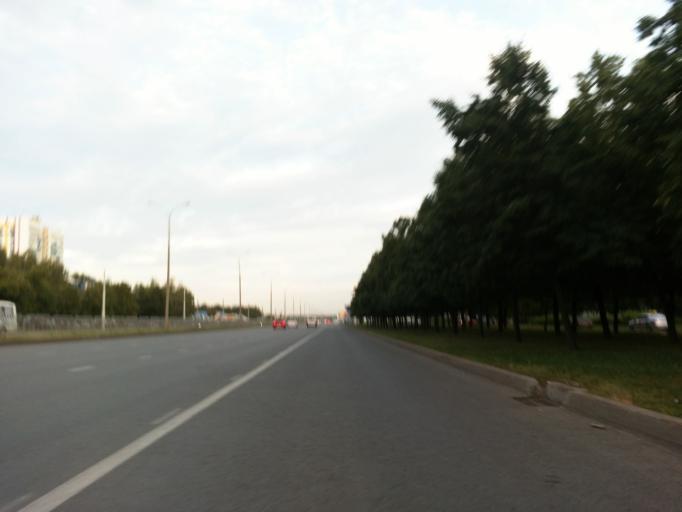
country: RU
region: Tatarstan
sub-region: Tukayevskiy Rayon
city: Naberezhnyye Chelny
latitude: 55.7444
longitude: 52.4253
